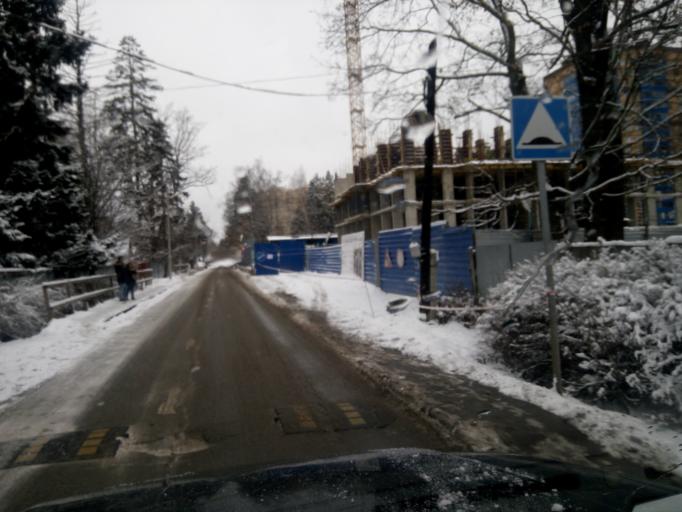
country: RU
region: Moskovskaya
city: Skhodnya
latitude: 55.9521
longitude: 37.3093
